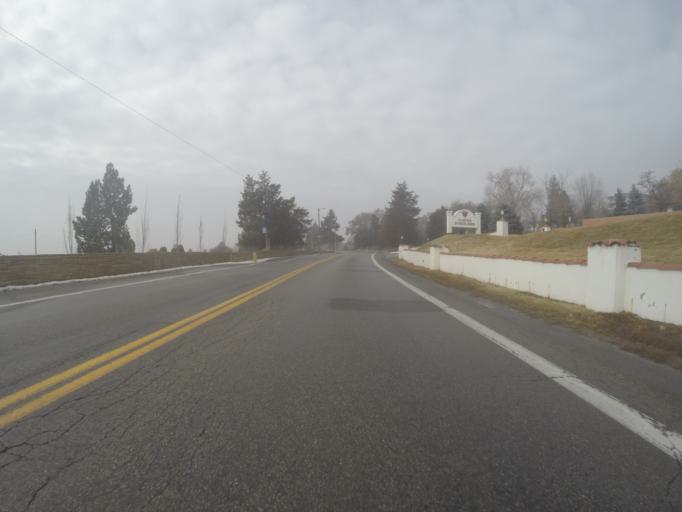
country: US
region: Utah
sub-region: Salt Lake County
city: Salt Lake City
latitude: 40.7806
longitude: -111.8600
